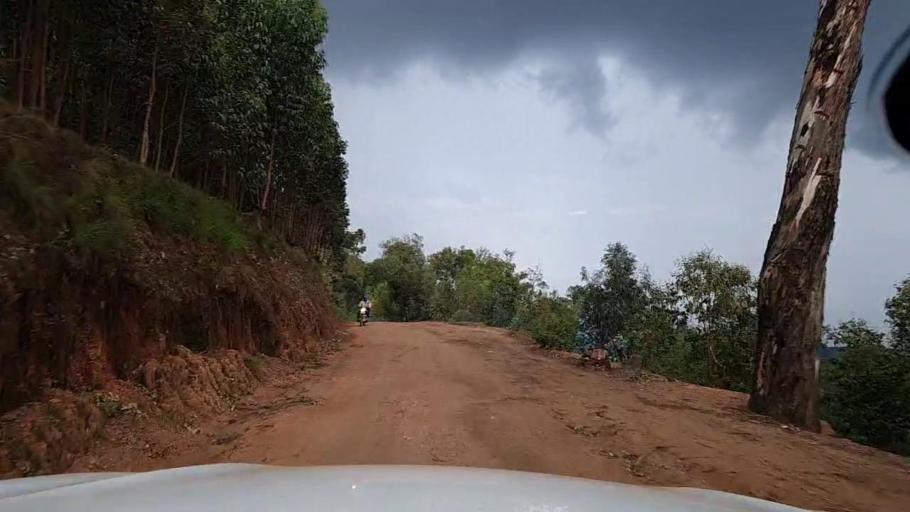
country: BI
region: Kayanza
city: Kayanza
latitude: -2.7907
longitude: 29.5254
